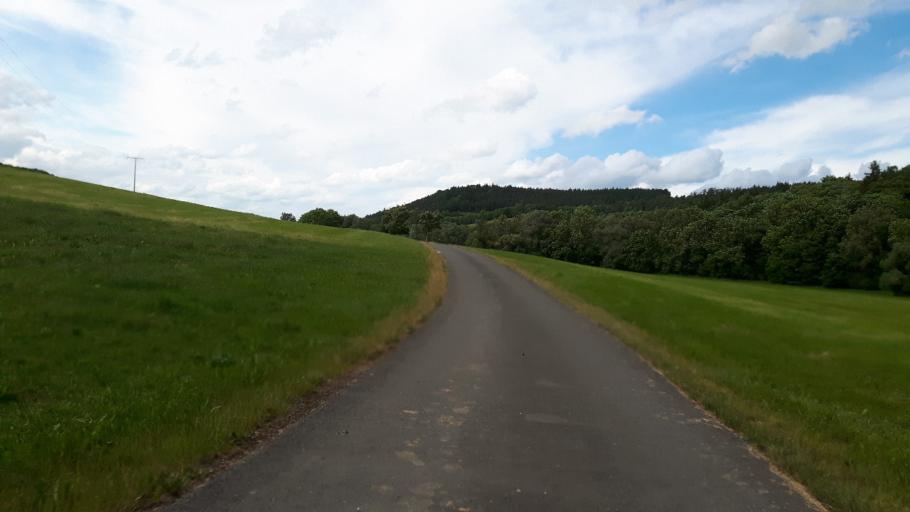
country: DE
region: Thuringia
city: Barchfeld
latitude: 50.8149
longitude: 11.1792
